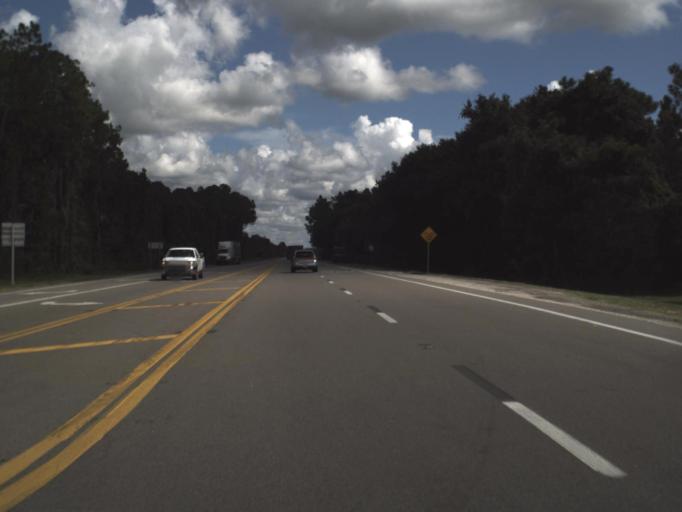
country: US
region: Florida
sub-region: Pasco County
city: Zephyrhills North
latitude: 28.2482
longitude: -82.0555
